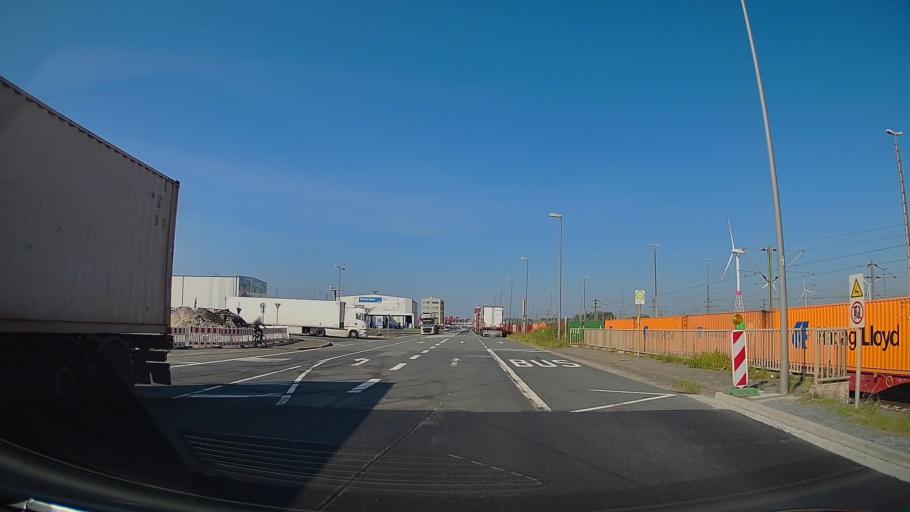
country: DE
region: Bremen
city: Bremerhaven
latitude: 53.5877
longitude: 8.5428
